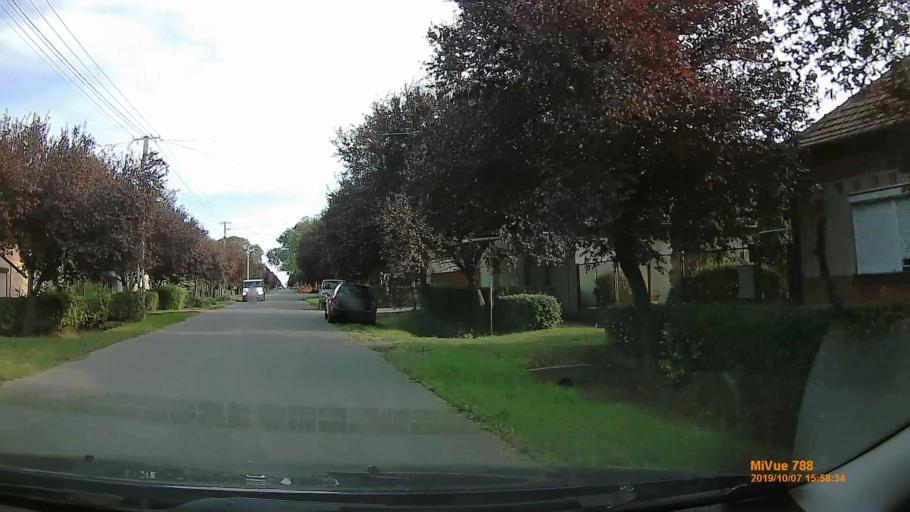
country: HU
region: Bekes
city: Szarvas
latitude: 46.8284
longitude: 20.6459
